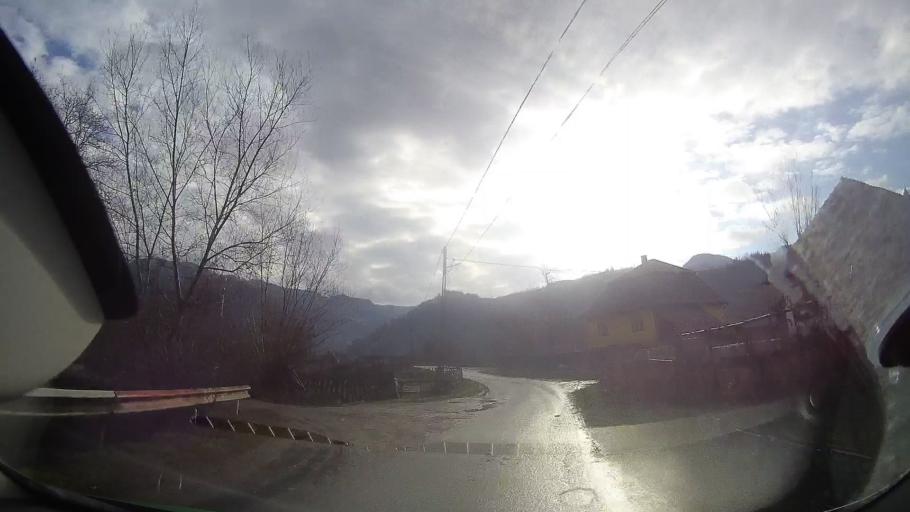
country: RO
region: Alba
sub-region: Comuna Ocolis
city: Ocolis
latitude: 46.4801
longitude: 23.4642
